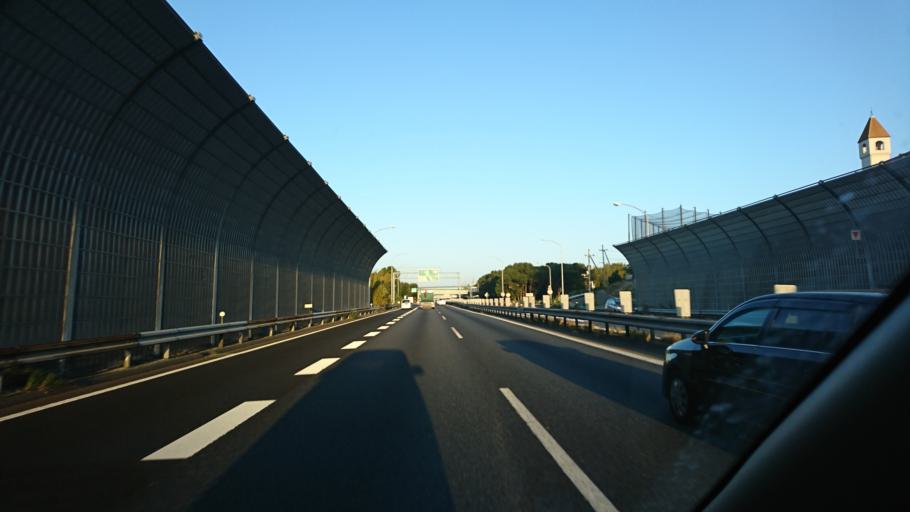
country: JP
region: Hyogo
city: Akashi
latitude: 34.7084
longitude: 134.9473
